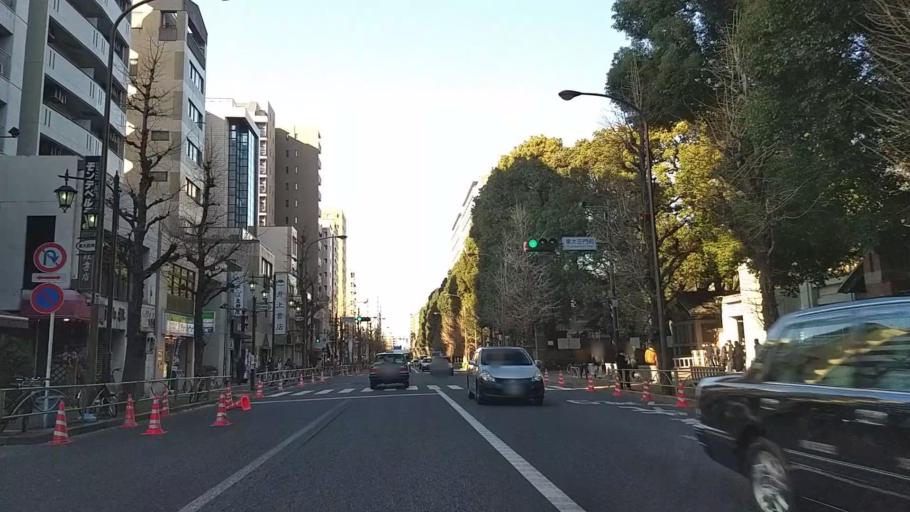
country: JP
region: Tokyo
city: Tokyo
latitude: 35.7127
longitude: 139.7595
